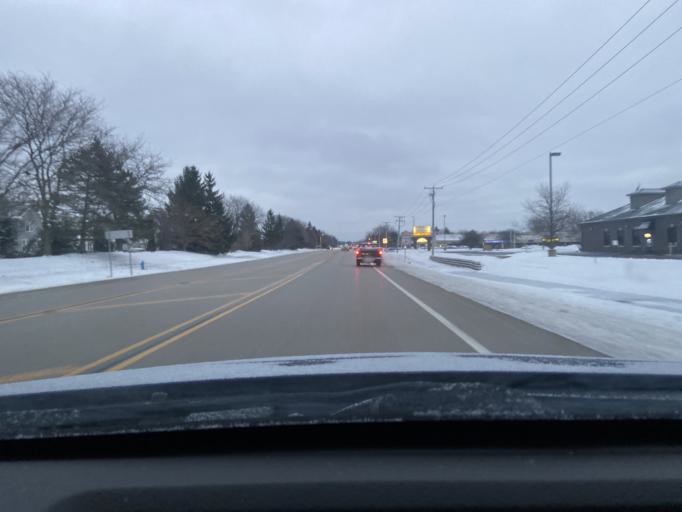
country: US
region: Illinois
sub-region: Lake County
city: Grayslake
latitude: 42.3445
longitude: -88.0223
